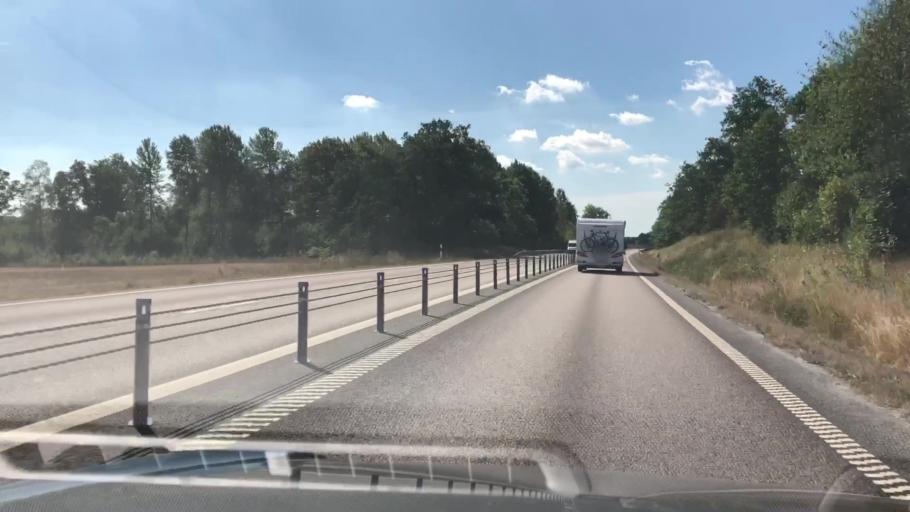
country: SE
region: Kalmar
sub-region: Kalmar Kommun
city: Lindsdal
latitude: 56.8161
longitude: 16.3694
